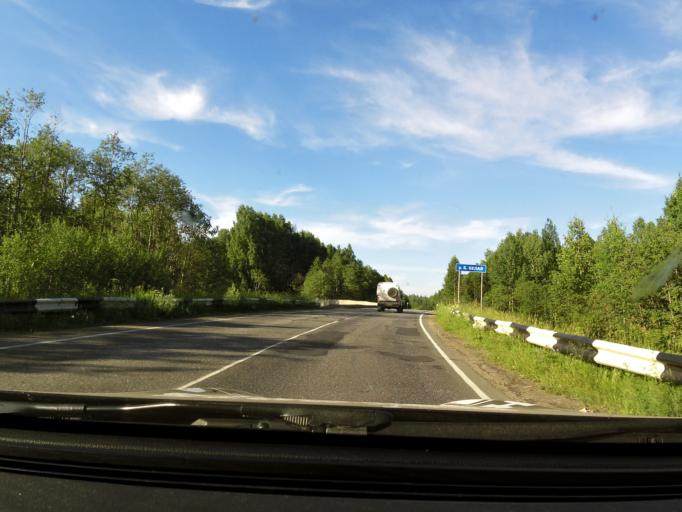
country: RU
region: Kirov
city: Belorechensk
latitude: 58.7647
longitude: 52.3610
